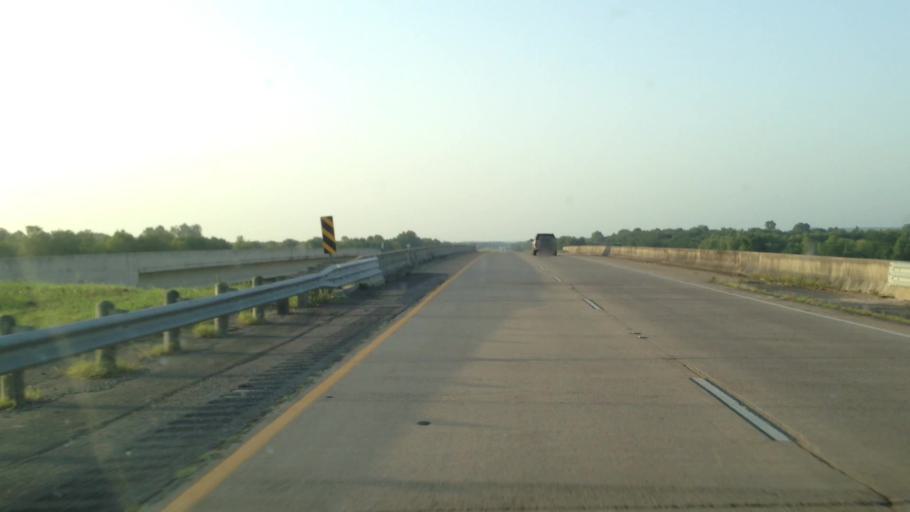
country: US
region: Louisiana
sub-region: Natchitoches Parish
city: Vienna Bend
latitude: 31.6098
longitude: -93.0504
